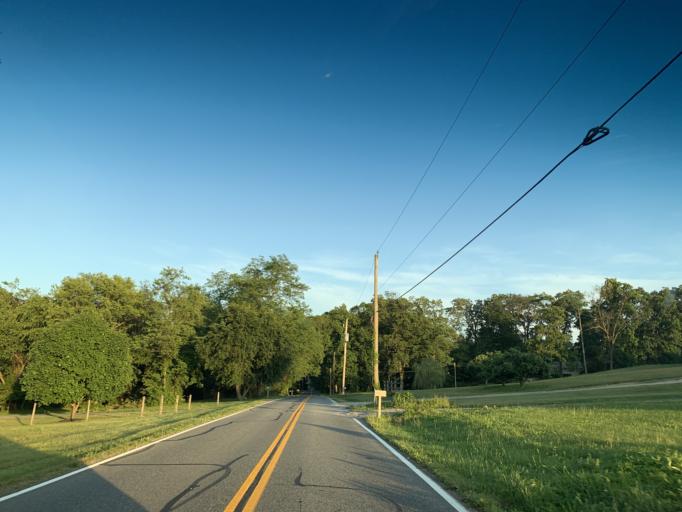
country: US
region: Maryland
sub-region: Cecil County
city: Rising Sun
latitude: 39.6335
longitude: -76.0715
